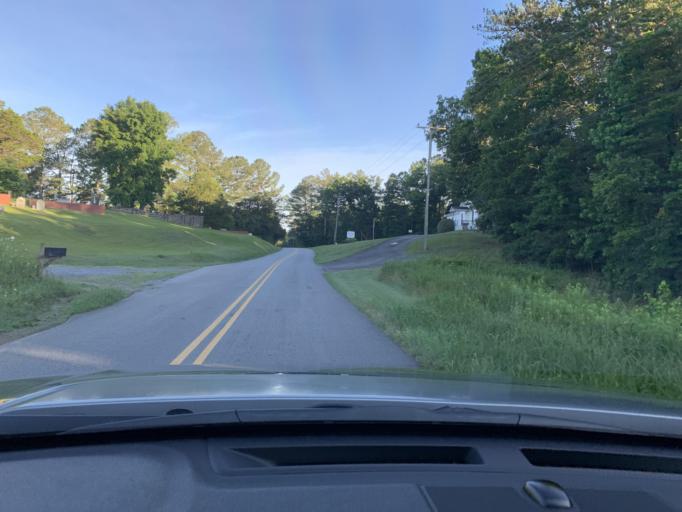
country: US
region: Georgia
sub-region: Bartow County
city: Rydal
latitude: 34.2593
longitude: -84.6981
